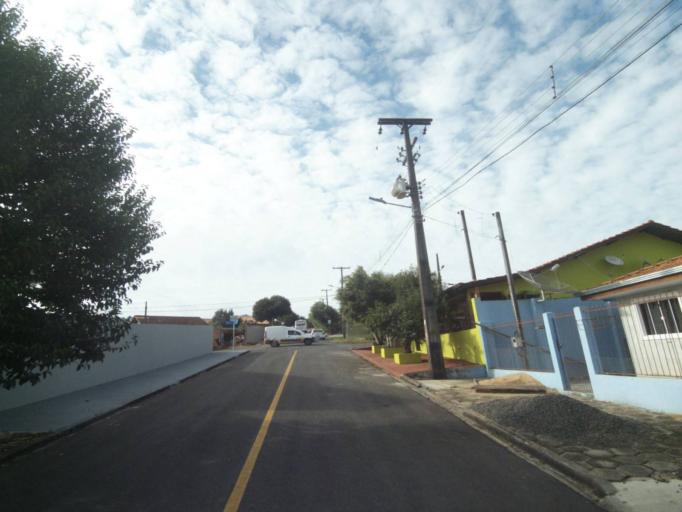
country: BR
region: Parana
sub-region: Telemaco Borba
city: Telemaco Borba
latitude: -24.3430
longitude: -50.6068
